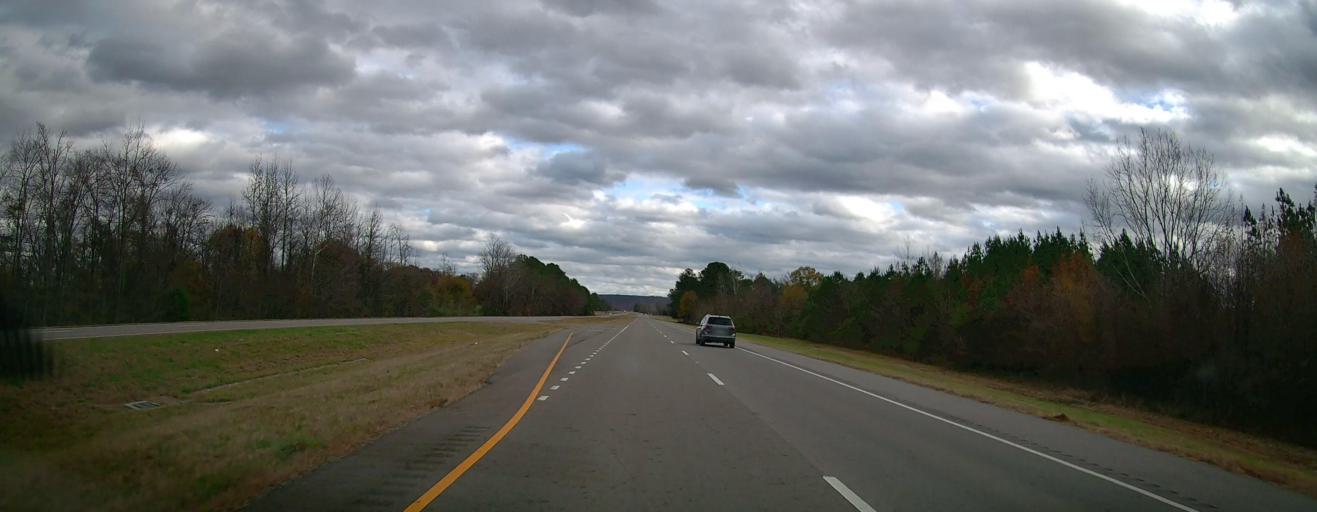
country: US
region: Alabama
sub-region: Morgan County
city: Danville
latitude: 34.3495
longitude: -87.0420
